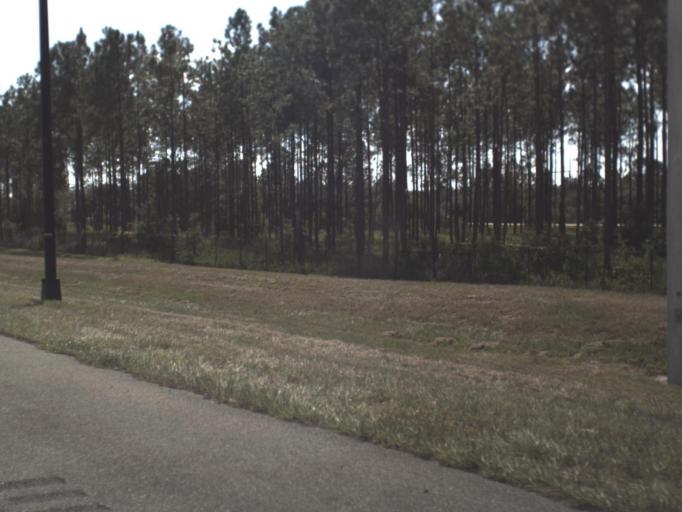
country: US
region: Florida
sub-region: Polk County
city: Citrus Ridge
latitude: 28.3918
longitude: -81.6185
